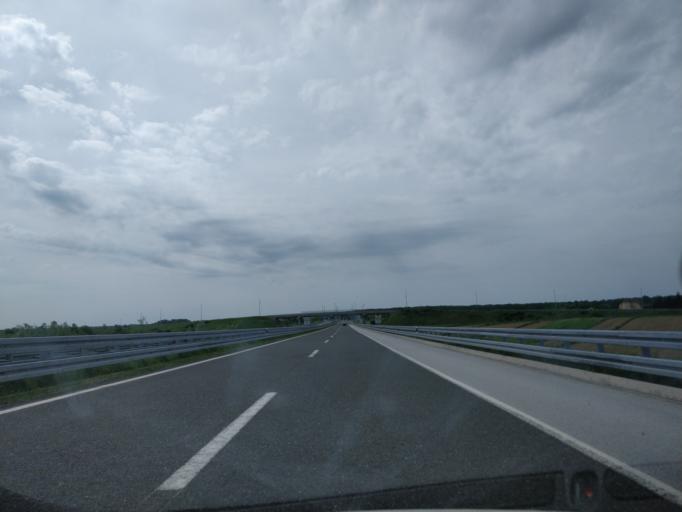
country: HR
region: Zagrebacka
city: Mraclin
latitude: 45.6723
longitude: 16.0786
